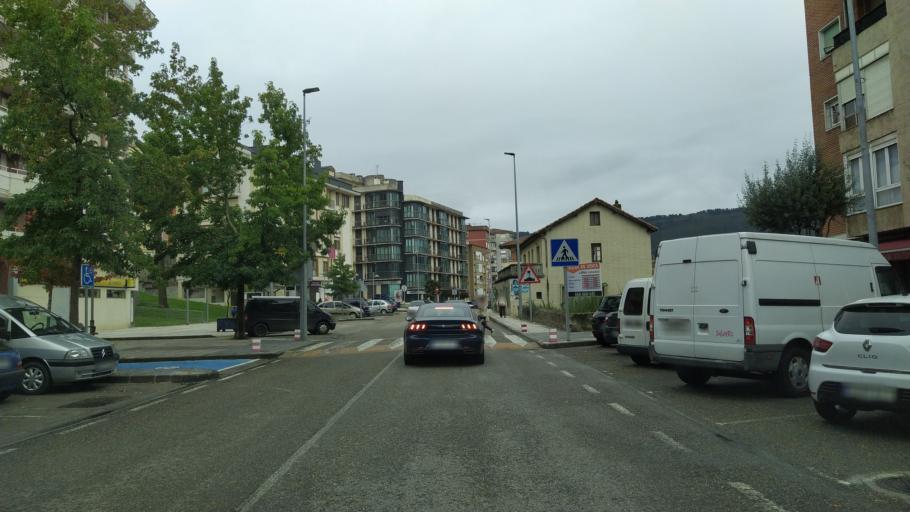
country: ES
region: Cantabria
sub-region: Provincia de Cantabria
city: El Astillero
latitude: 43.4000
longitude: -3.8238
